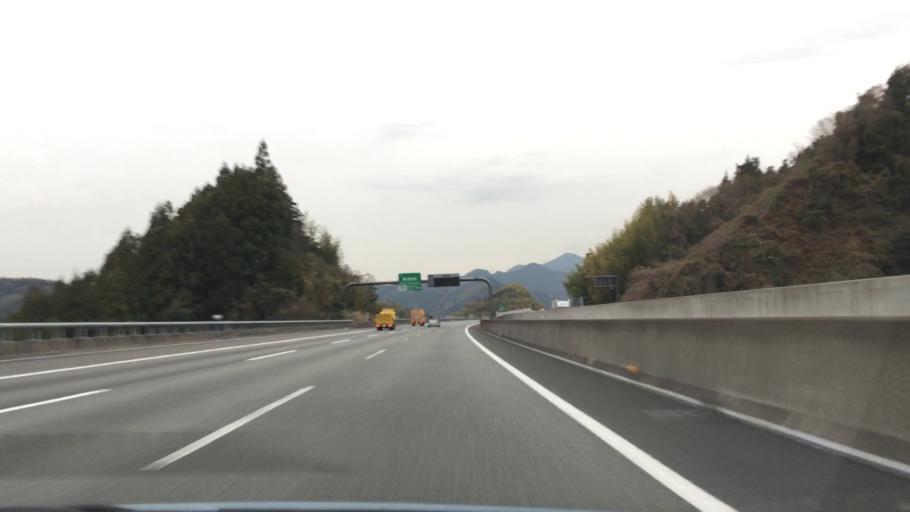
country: JP
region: Shizuoka
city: Shizuoka-shi
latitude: 35.0433
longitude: 138.3986
